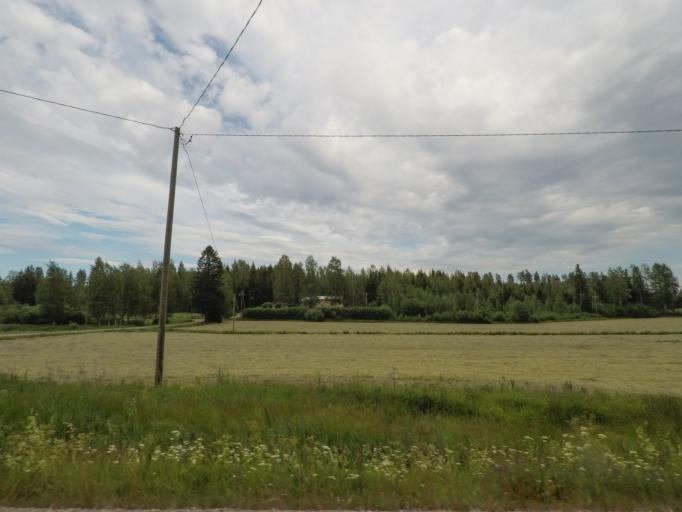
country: FI
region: Uusimaa
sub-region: Porvoo
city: Pukkila
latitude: 60.7754
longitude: 25.4535
